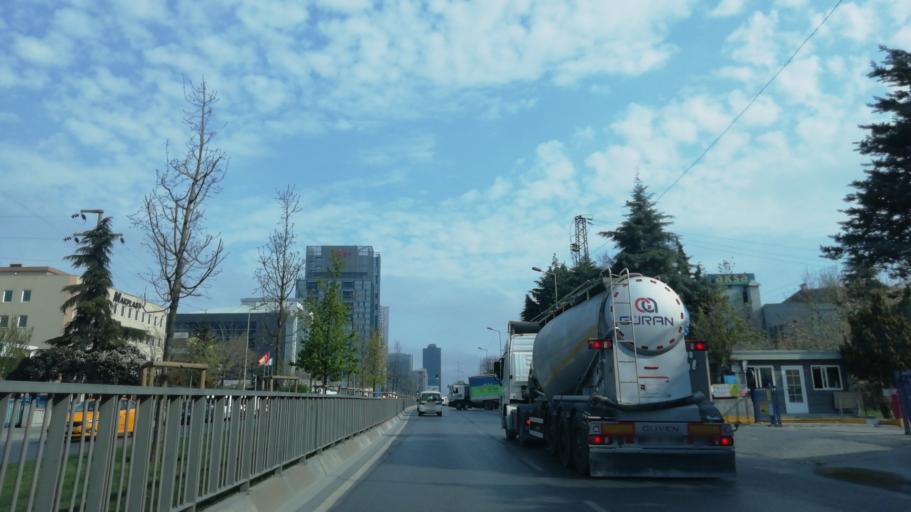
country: TR
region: Istanbul
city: Mahmutbey
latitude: 41.0481
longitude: 28.8123
